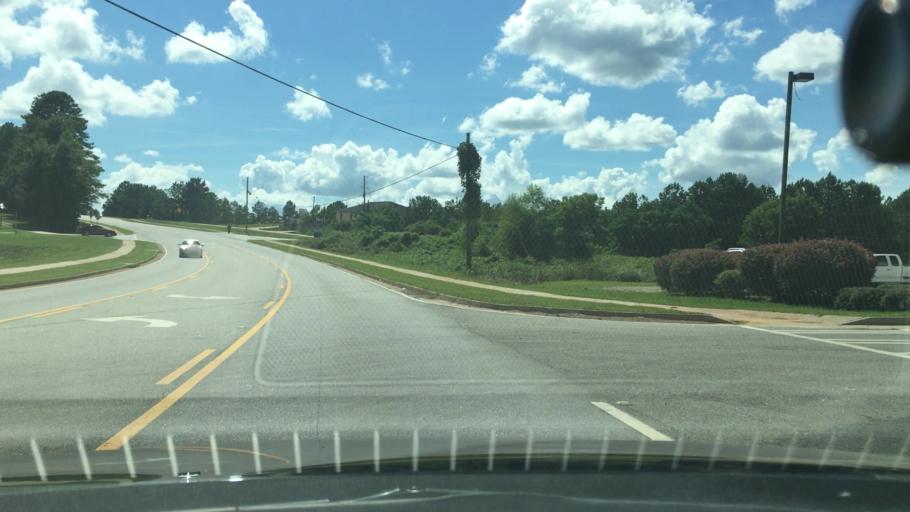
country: US
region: Georgia
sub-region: Jasper County
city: Monticello
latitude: 33.3054
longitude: -83.6990
